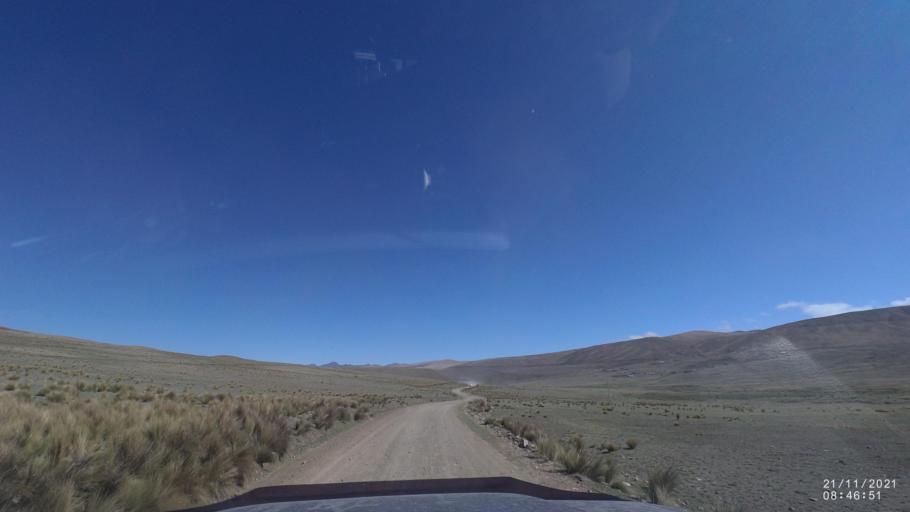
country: BO
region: Cochabamba
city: Cochabamba
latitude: -17.2402
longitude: -66.2333
